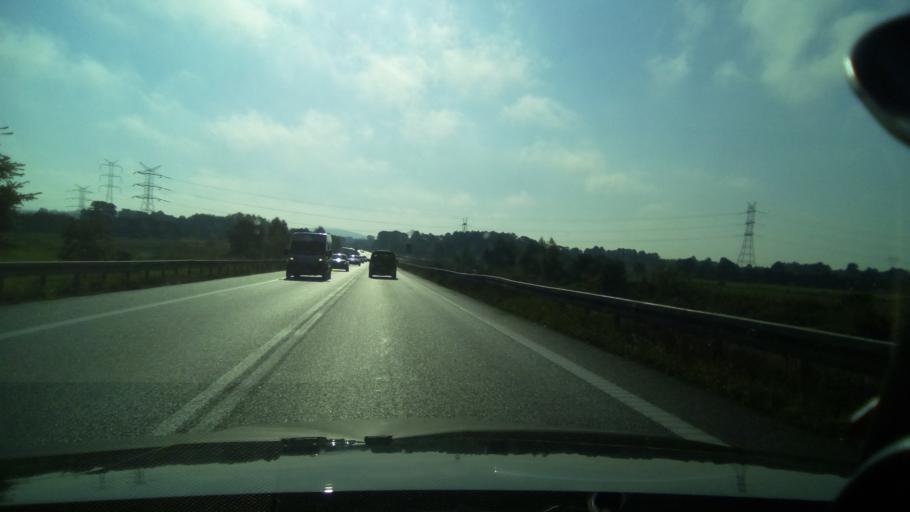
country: PL
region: Silesian Voivodeship
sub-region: Powiat bedzinski
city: Mierzecice
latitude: 50.4229
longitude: 19.1818
